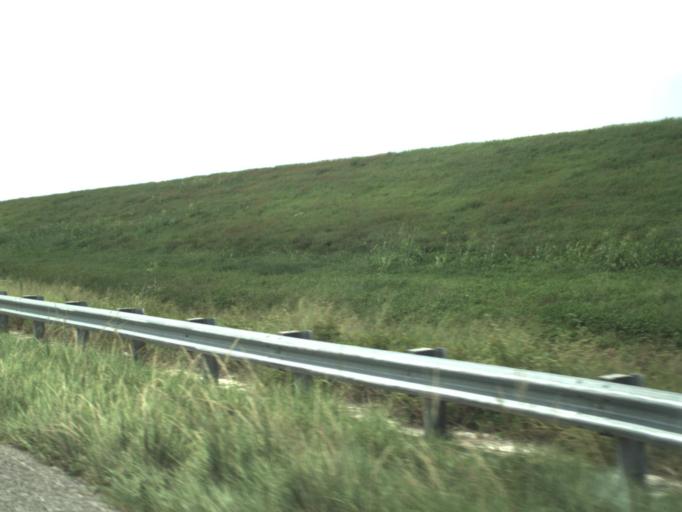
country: US
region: Florida
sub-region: Hendry County
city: Clewiston
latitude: 26.7336
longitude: -80.8647
